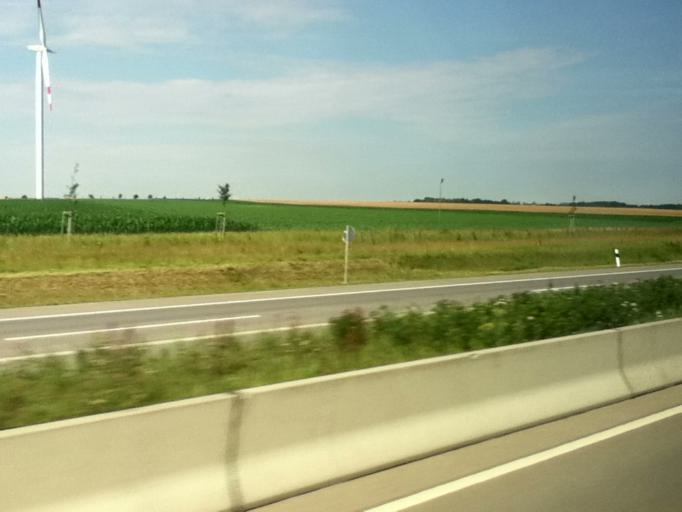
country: DE
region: Thuringia
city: Heyersdorf
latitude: 50.8408
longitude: 12.3559
